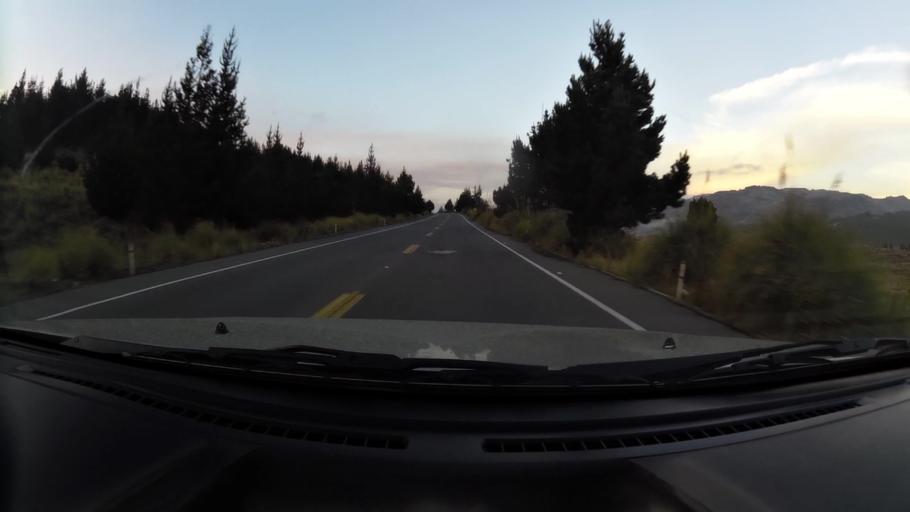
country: EC
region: Chimborazo
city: Alausi
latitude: -2.0419
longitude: -78.7382
